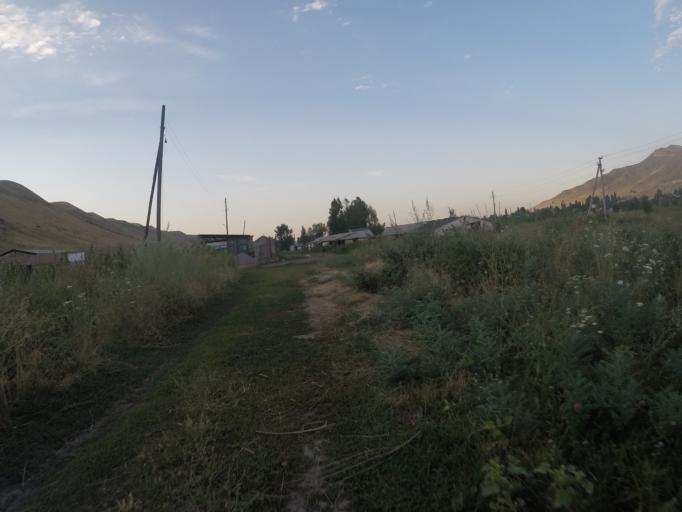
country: KG
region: Chuy
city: Bishkek
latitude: 42.7634
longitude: 74.6378
